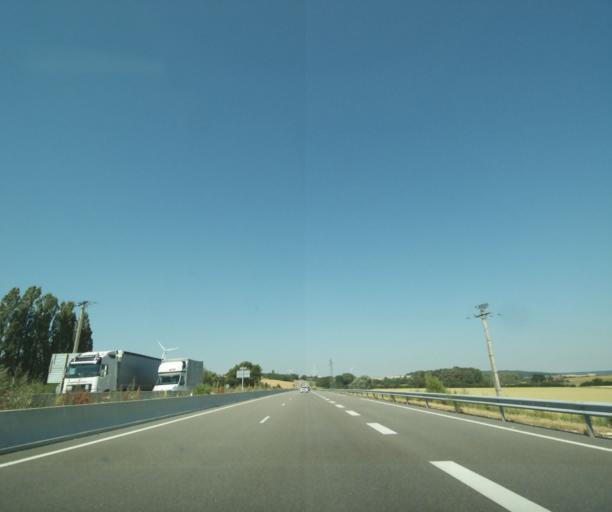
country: FR
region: Lorraine
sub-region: Departement de la Meuse
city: Lerouville
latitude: 48.7053
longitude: 5.4619
